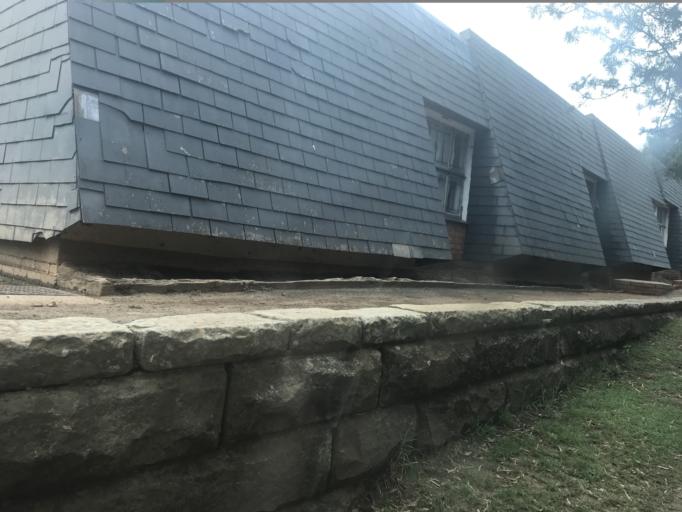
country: LS
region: Maseru
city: Nako
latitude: -29.6276
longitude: 27.5096
